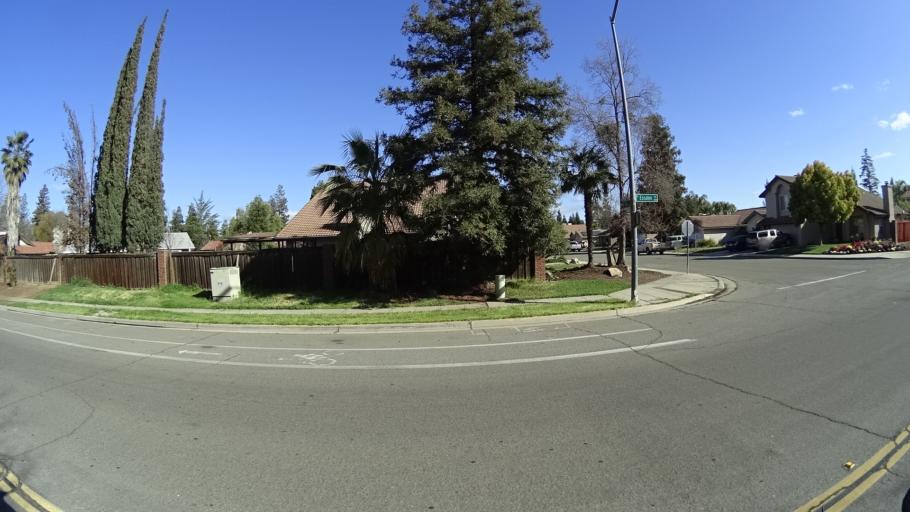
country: US
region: California
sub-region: Fresno County
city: West Park
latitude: 36.8263
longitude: -119.8828
